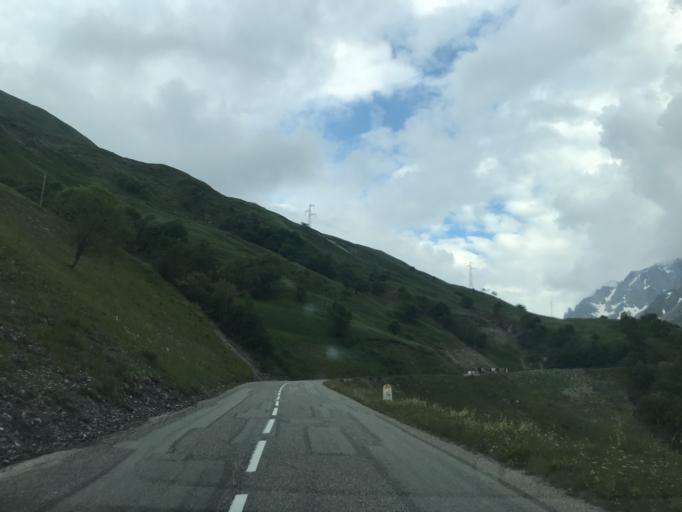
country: FR
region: Rhone-Alpes
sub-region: Departement de la Savoie
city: Valloire
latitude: 45.1029
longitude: 6.4281
